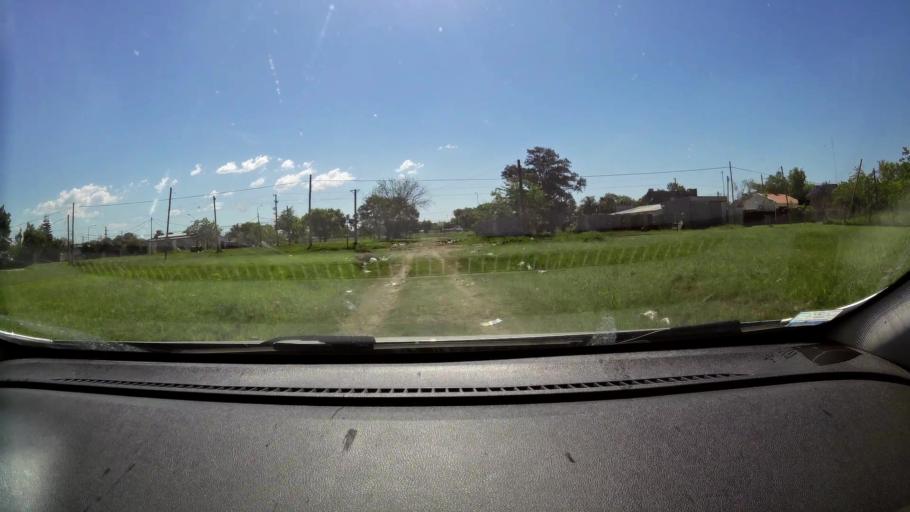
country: AR
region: Santa Fe
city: Santa Fe de la Vera Cruz
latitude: -31.5982
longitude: -60.6725
